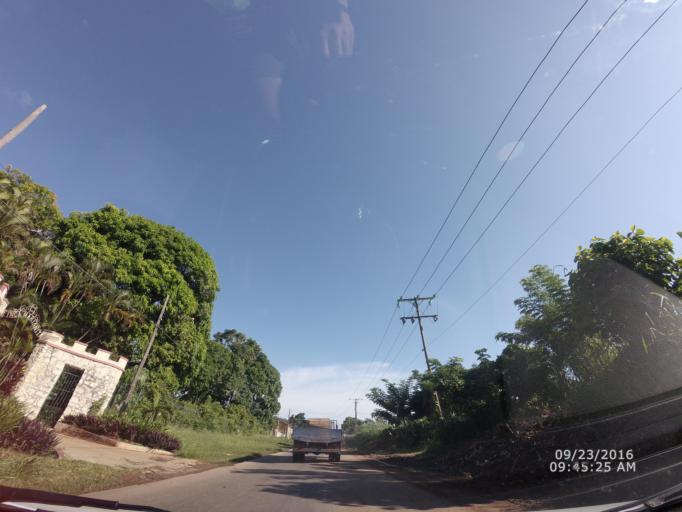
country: CU
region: La Habana
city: Santiago de las Vegas
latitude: 22.9509
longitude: -82.4105
